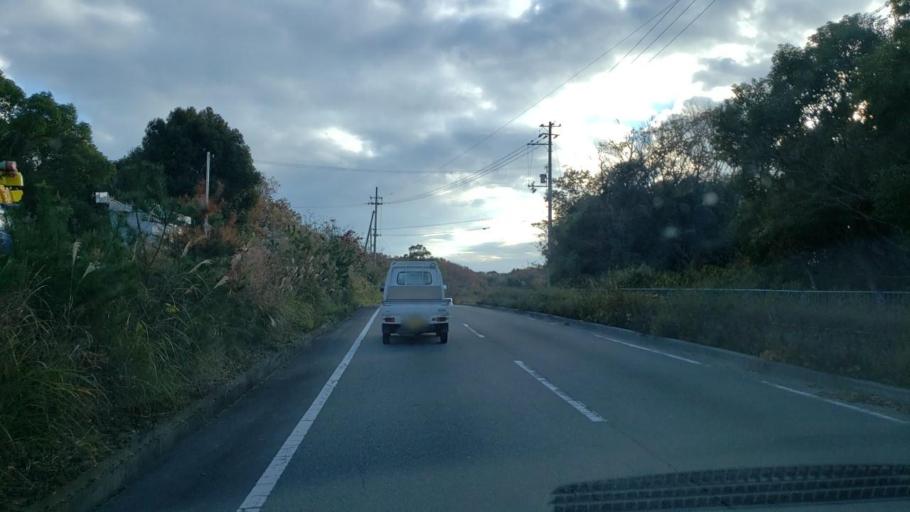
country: JP
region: Hyogo
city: Akashi
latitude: 34.5740
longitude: 134.9799
